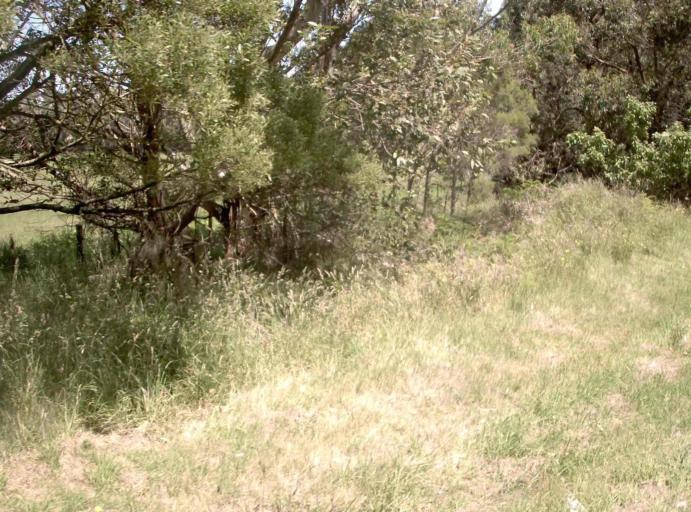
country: AU
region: Victoria
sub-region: Bass Coast
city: North Wonthaggi
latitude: -38.7708
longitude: 146.0645
